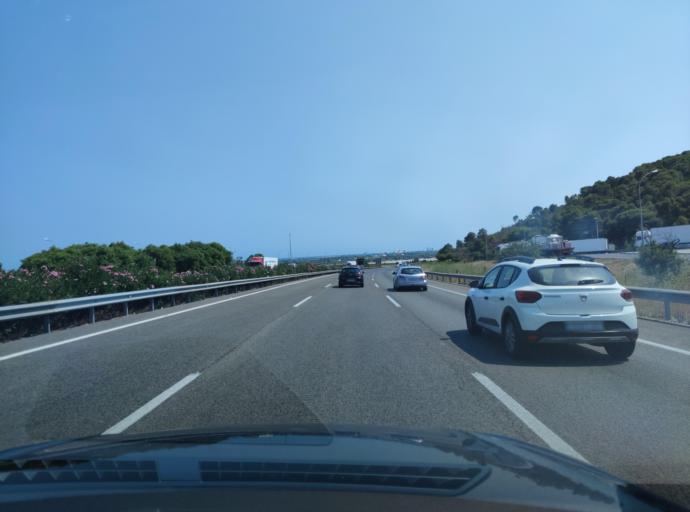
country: ES
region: Valencia
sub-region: Provincia de Valencia
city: Pucol
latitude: 39.6498
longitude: -0.3019
